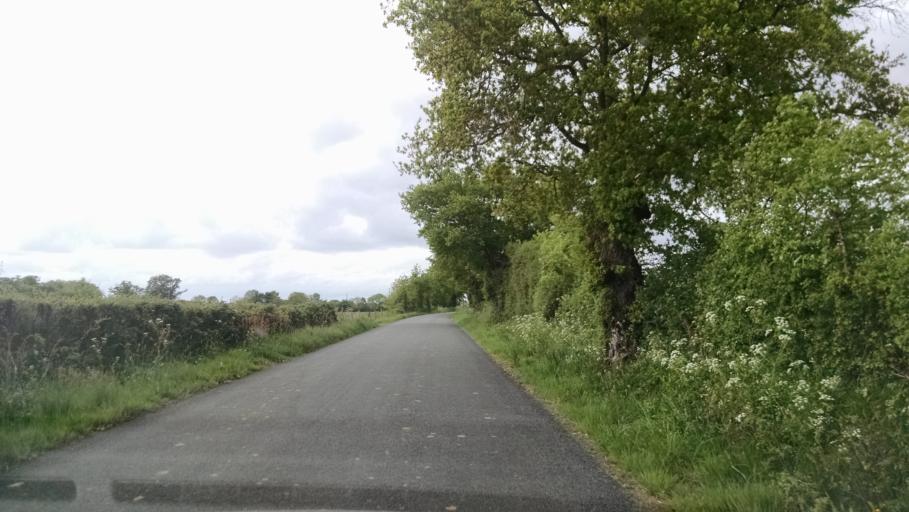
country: FR
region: Pays de la Loire
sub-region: Departement de la Vendee
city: Saint-Hilaire-de-Loulay
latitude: 46.9852
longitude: -1.3372
